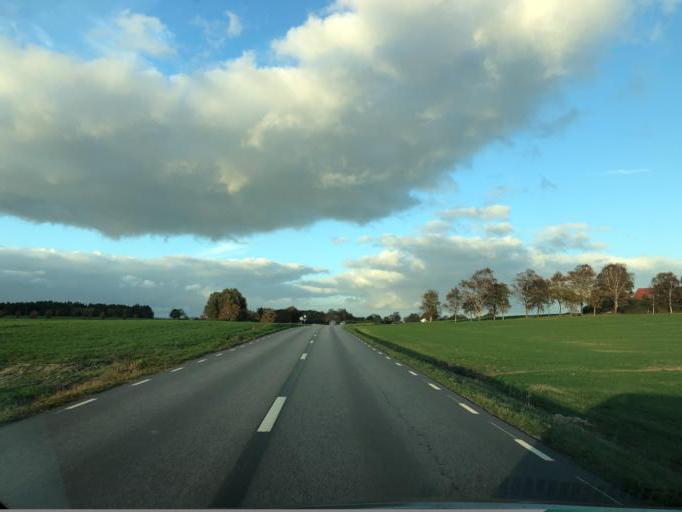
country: SE
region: Skane
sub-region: Svalovs Kommun
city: Teckomatorp
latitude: 55.8498
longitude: 13.1191
